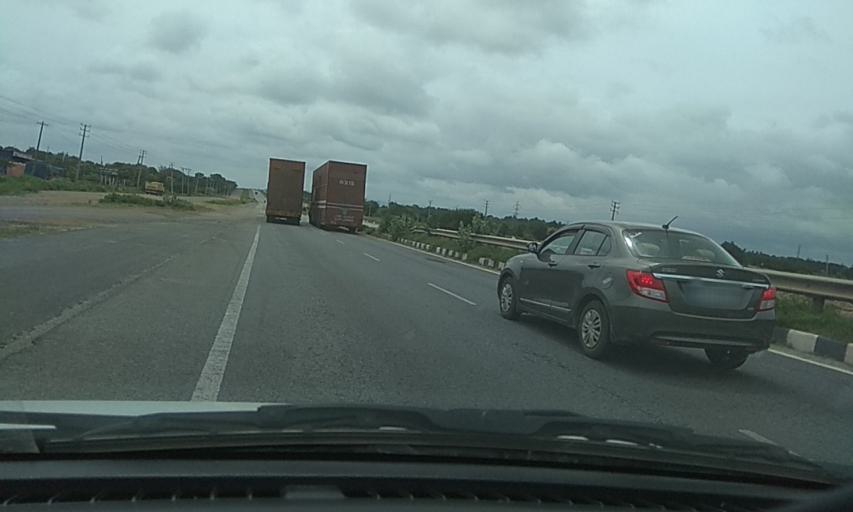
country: IN
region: Karnataka
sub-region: Davanagere
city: Mayakonda
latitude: 14.3082
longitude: 76.2523
